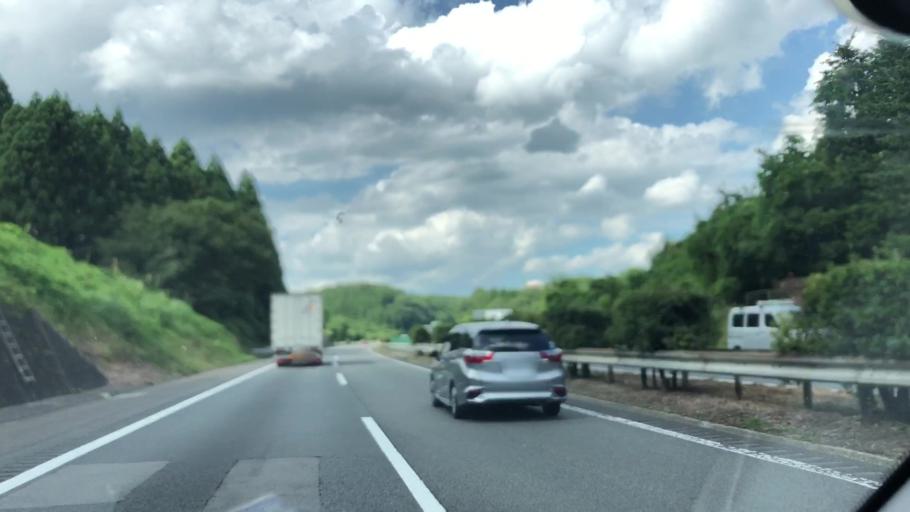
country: JP
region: Tochigi
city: Kuroiso
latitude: 37.0638
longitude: 140.1069
